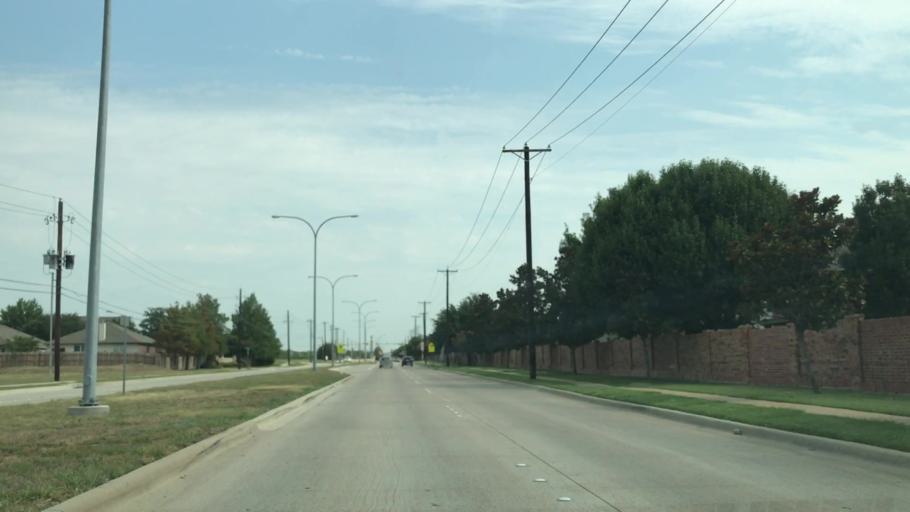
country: US
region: Texas
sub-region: Tarrant County
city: Keller
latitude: 32.8987
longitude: -97.2725
